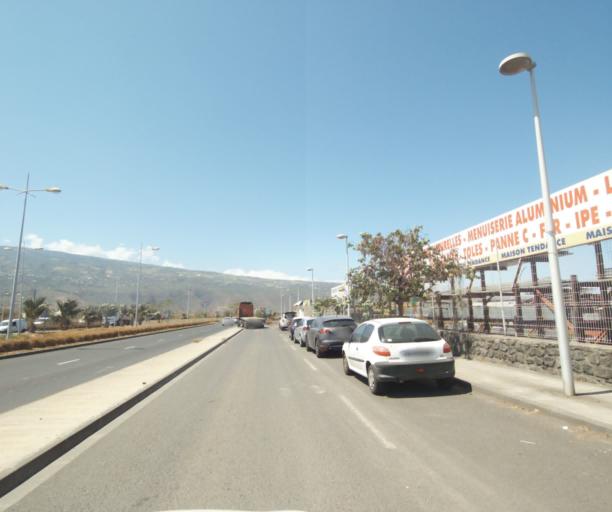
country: RE
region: Reunion
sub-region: Reunion
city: Le Port
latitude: -20.9700
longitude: 55.2956
